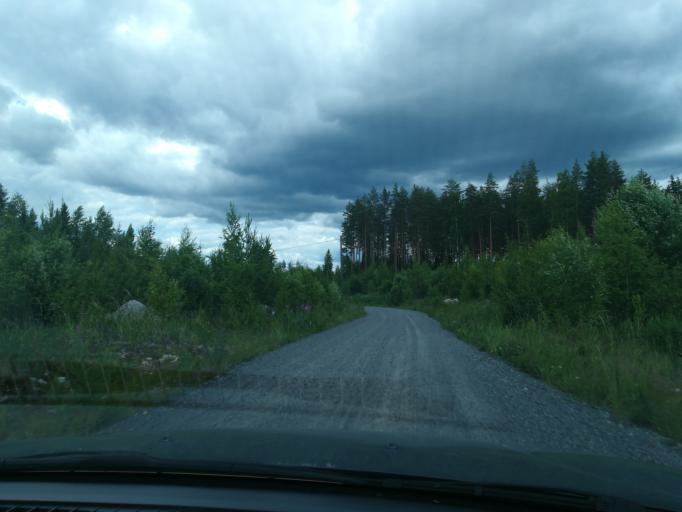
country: FI
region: Southern Savonia
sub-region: Mikkeli
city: Mikkeli
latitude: 61.6648
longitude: 27.1183
